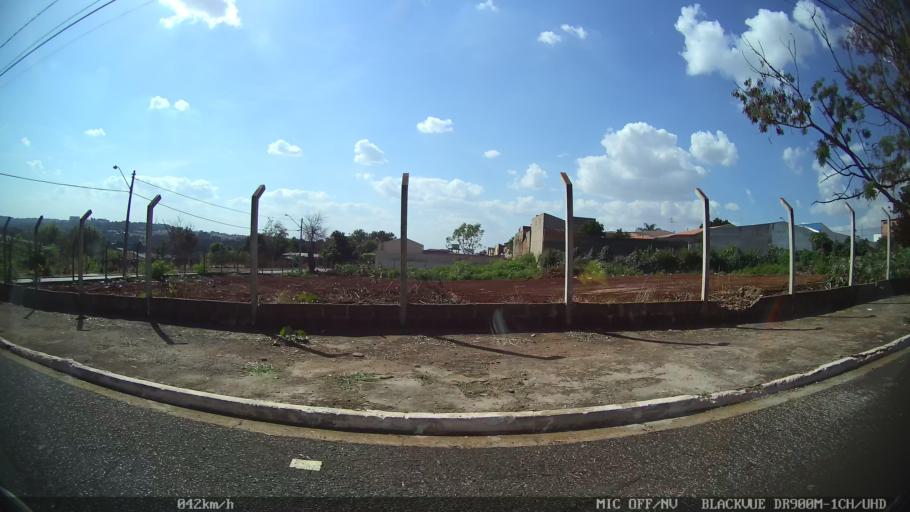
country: BR
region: Sao Paulo
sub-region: Ribeirao Preto
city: Ribeirao Preto
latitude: -21.1852
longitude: -47.8394
